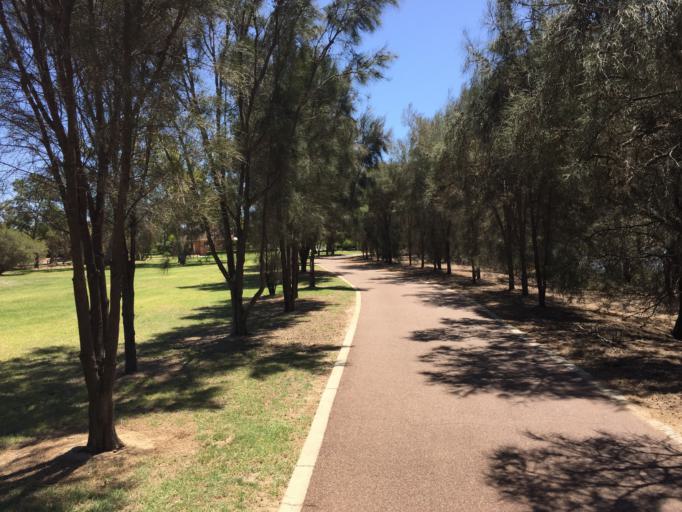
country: AU
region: Western Australia
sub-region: Canning
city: Wilson
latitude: -32.0242
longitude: 115.8994
